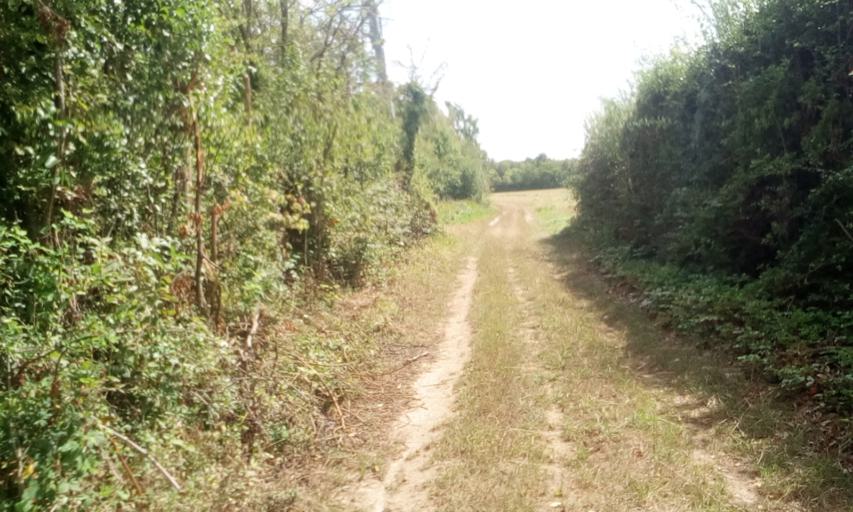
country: FR
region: Lower Normandy
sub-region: Departement du Calvados
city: Cagny
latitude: 49.1111
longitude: -0.2509
